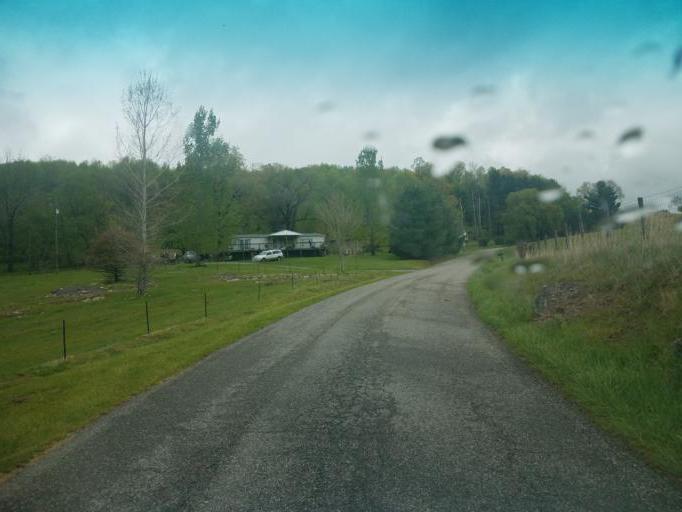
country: US
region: Virginia
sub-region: Smyth County
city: Marion
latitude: 36.9384
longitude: -81.5219
